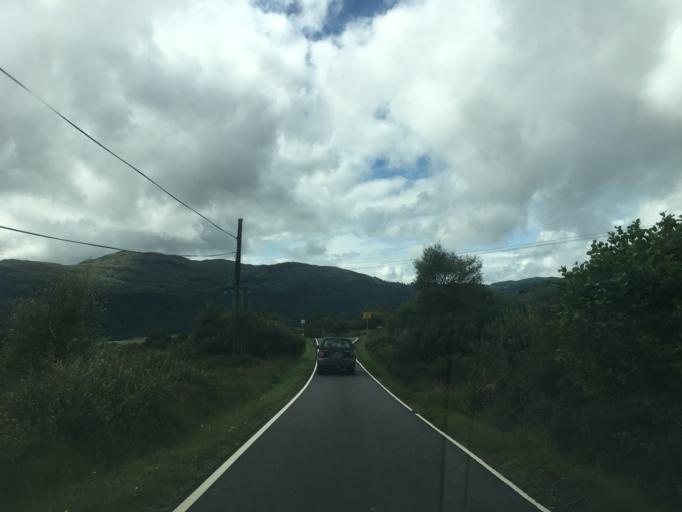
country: GB
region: Scotland
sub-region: Argyll and Bute
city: Port Bannatyne
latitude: 55.9880
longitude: -5.1667
